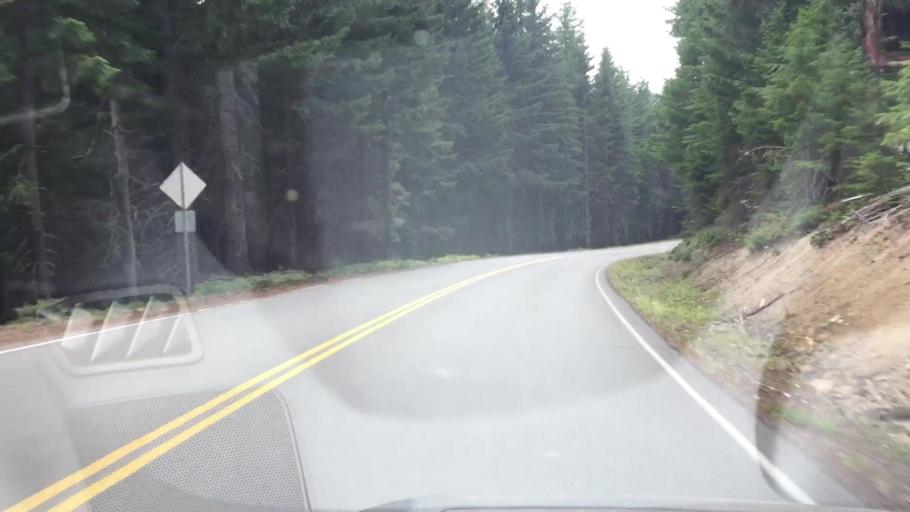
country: US
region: Washington
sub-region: Klickitat County
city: White Salmon
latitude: 46.1421
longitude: -121.6282
